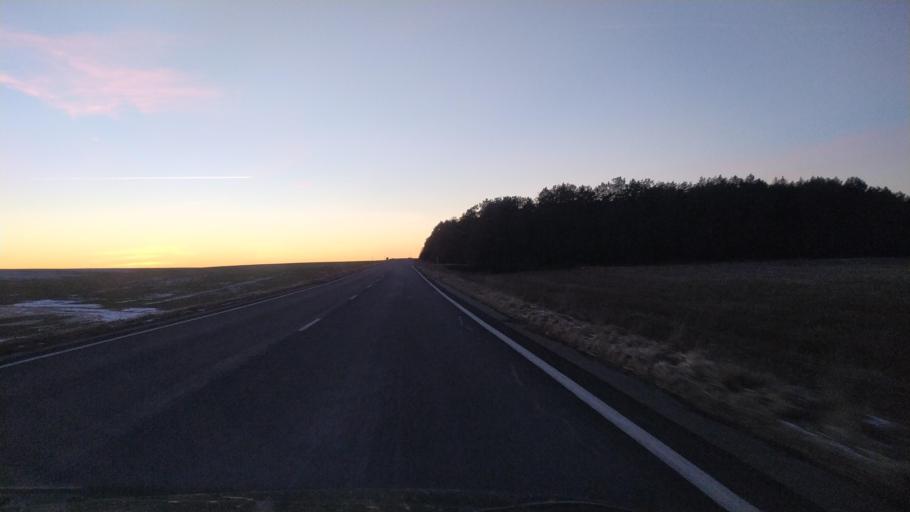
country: BY
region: Brest
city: Kamyanyets
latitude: 52.3927
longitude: 23.9640
